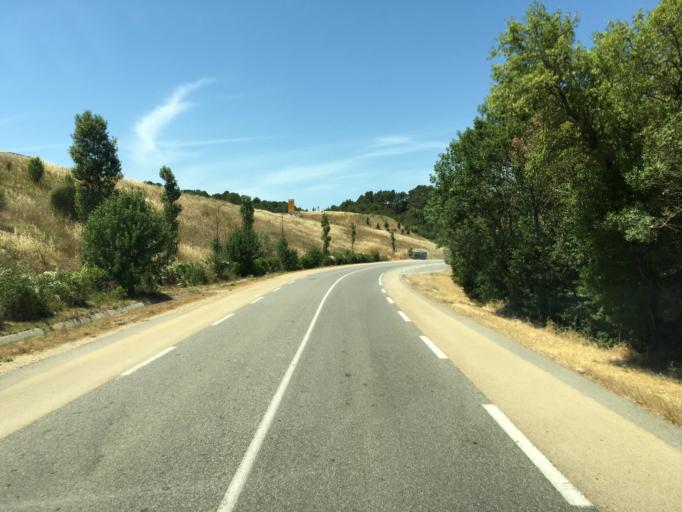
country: FR
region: Provence-Alpes-Cote d'Azur
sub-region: Departement du Var
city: Saint-Maximin-la-Sainte-Baume
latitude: 43.4693
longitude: 5.8384
